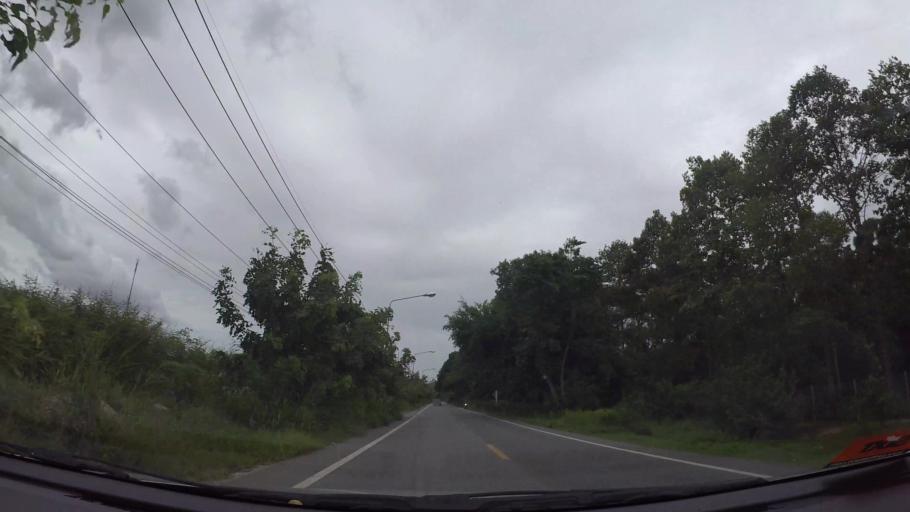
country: TH
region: Chon Buri
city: Si Racha
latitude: 13.1862
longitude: 100.9910
